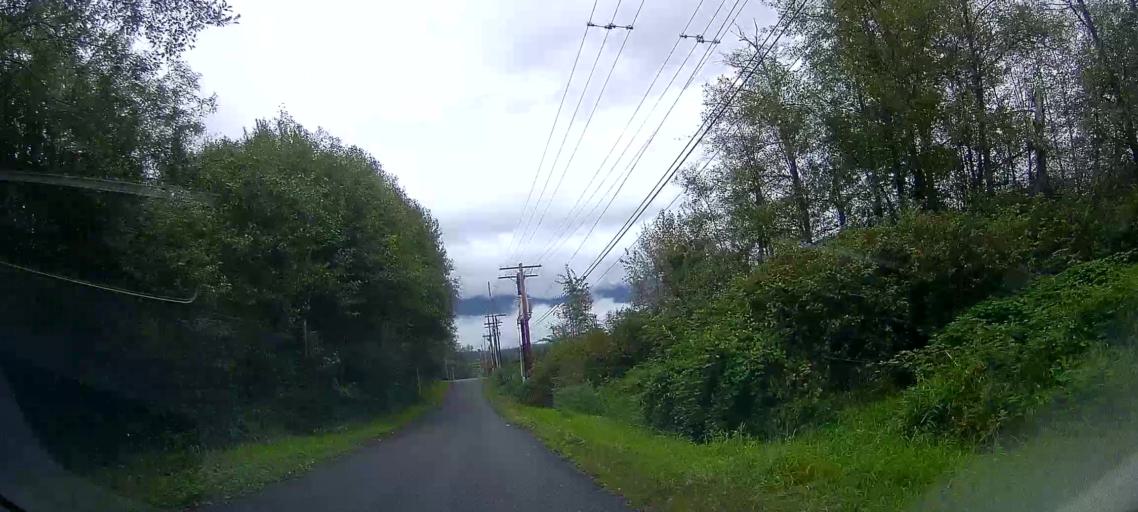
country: US
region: Washington
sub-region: Skagit County
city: Sedro-Woolley
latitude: 48.5271
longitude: -122.0062
